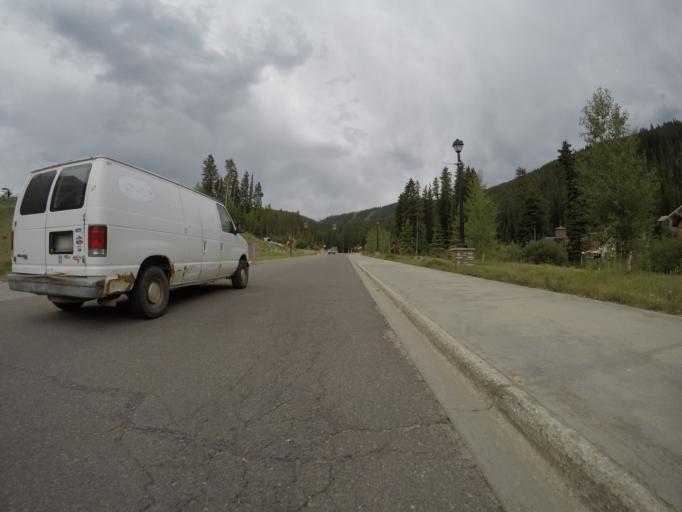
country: US
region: Colorado
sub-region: Grand County
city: Fraser
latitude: 39.8849
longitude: -105.7613
